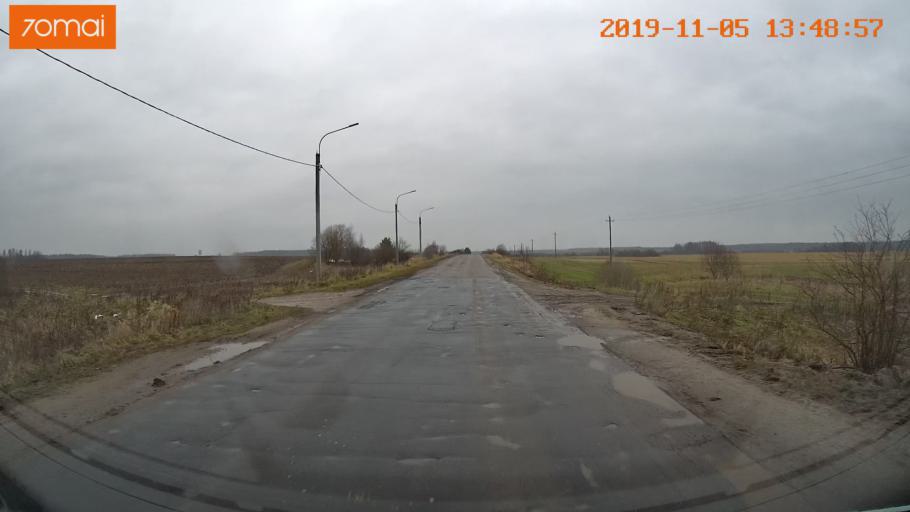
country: RU
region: Ivanovo
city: Shuya
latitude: 57.0062
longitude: 41.4078
